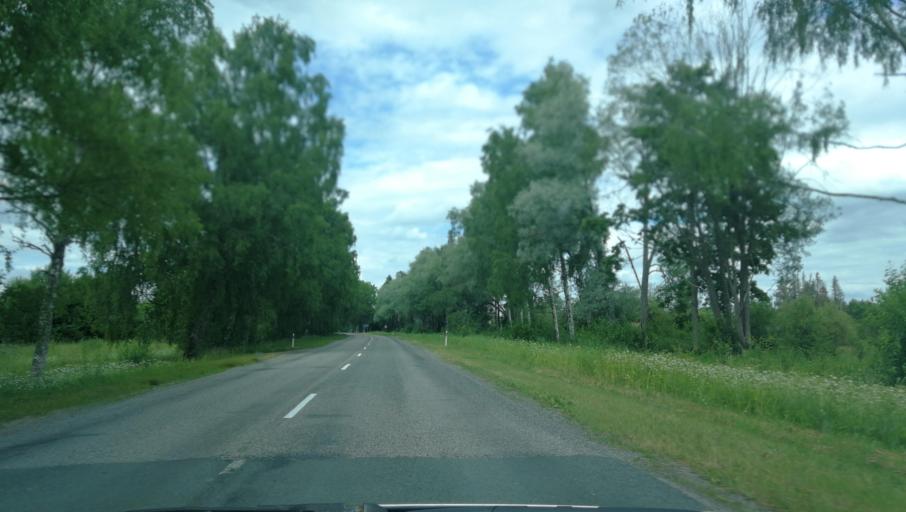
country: LV
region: Rujienas
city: Rujiena
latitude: 57.8530
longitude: 25.3783
